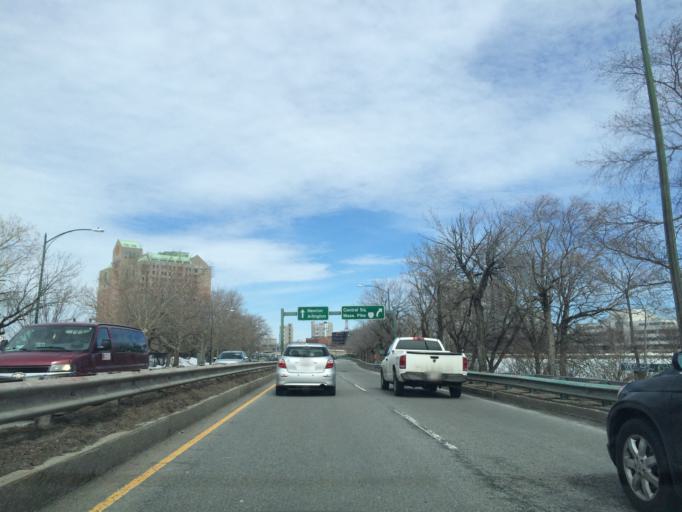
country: US
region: Massachusetts
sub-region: Middlesex County
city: Cambridge
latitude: 42.3573
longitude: -71.1181
